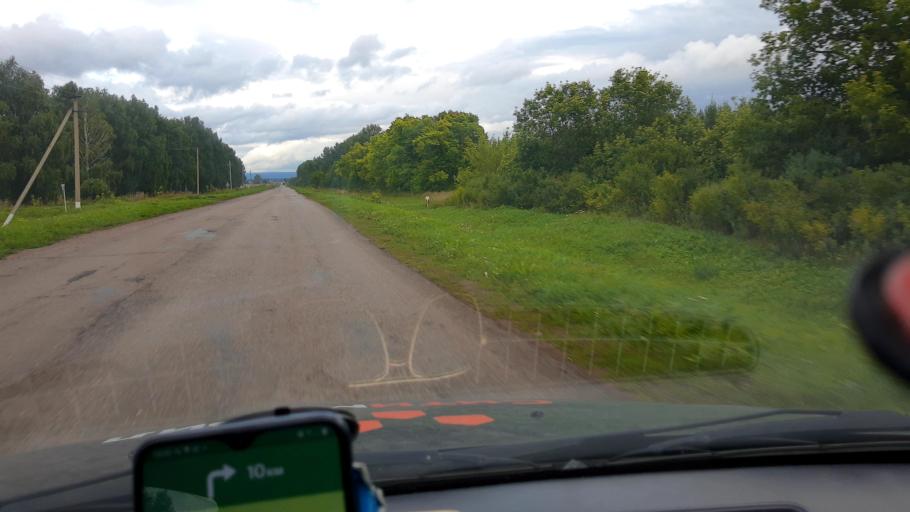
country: RU
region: Bashkortostan
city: Tolbazy
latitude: 53.9840
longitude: 56.2424
